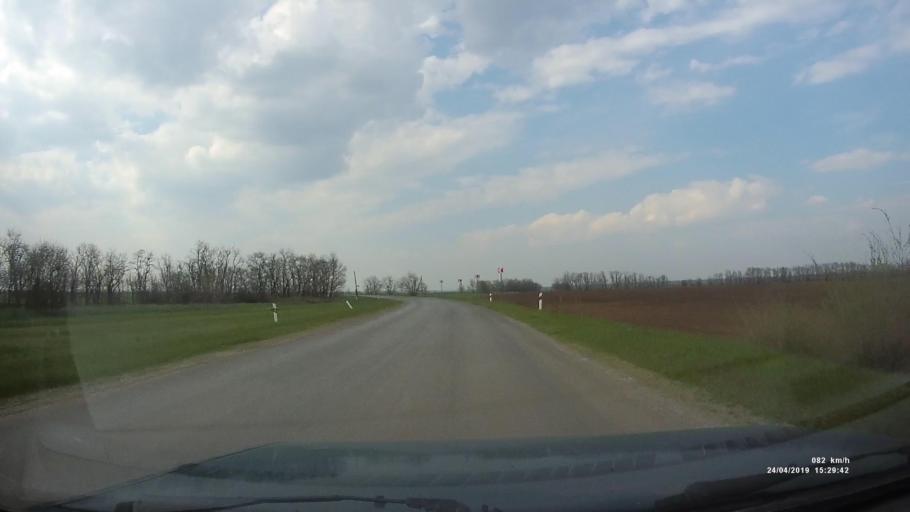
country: RU
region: Rostov
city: Remontnoye
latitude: 46.5962
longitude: 43.0158
